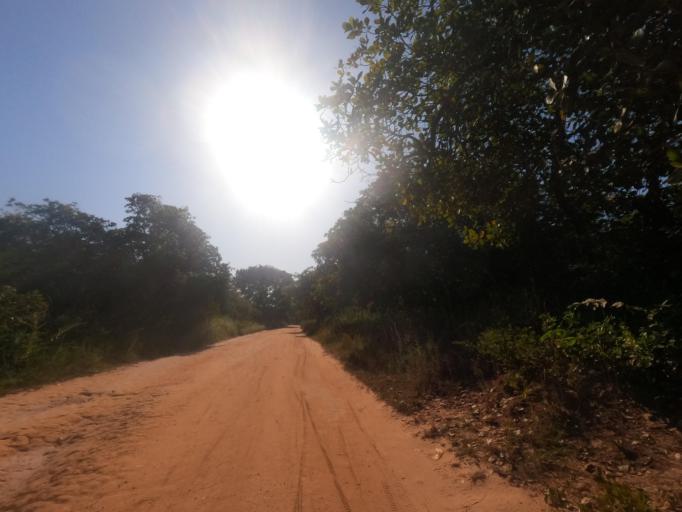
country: GW
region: Cacheu
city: Cacheu
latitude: 12.4001
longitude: -16.2085
